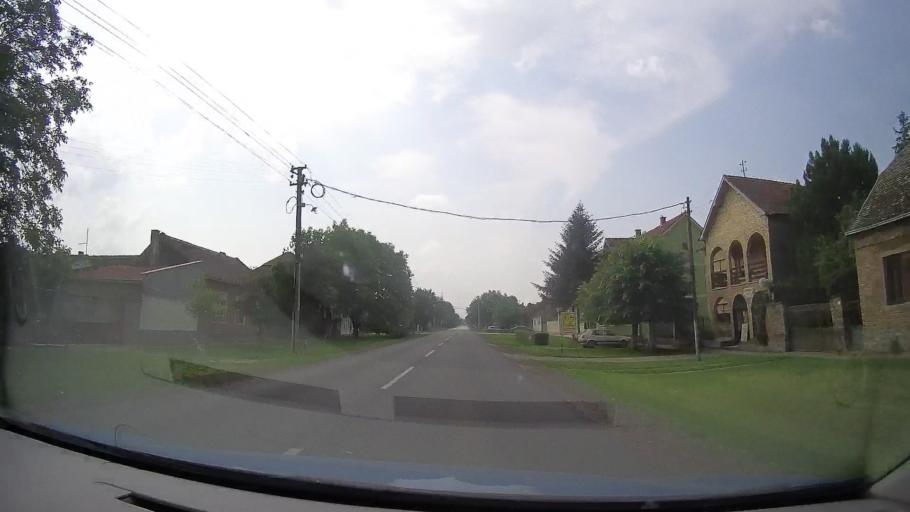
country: RS
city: Crepaja
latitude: 45.0171
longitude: 20.6343
